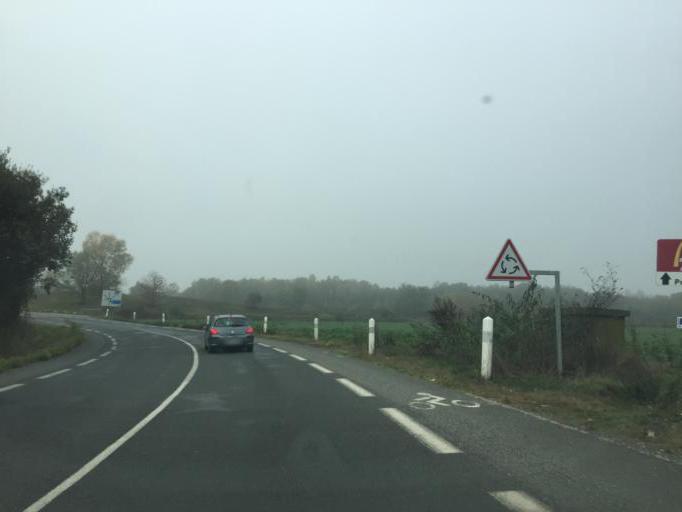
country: FR
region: Rhone-Alpes
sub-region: Departement du Rhone
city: Rillieux-la-Pape
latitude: 45.8246
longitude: 4.9207
